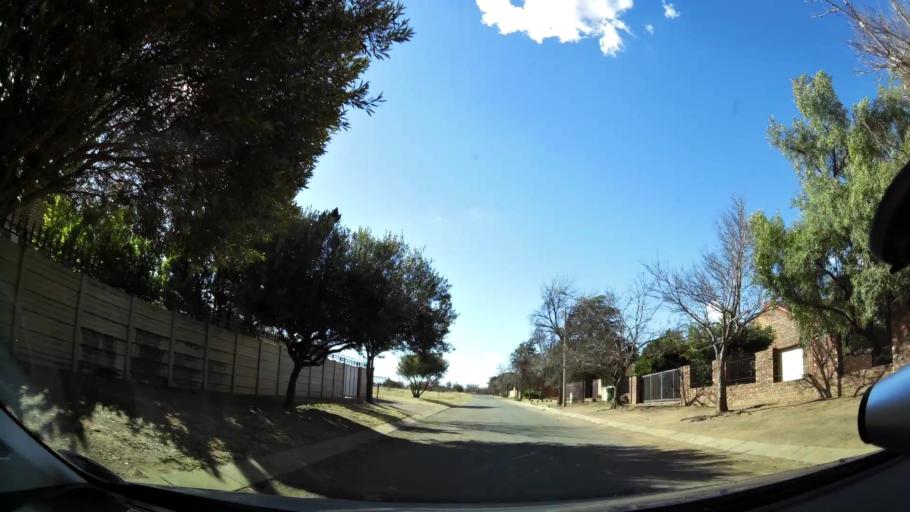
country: ZA
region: North-West
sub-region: Dr Kenneth Kaunda District Municipality
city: Klerksdorp
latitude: -26.8318
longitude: 26.6528
